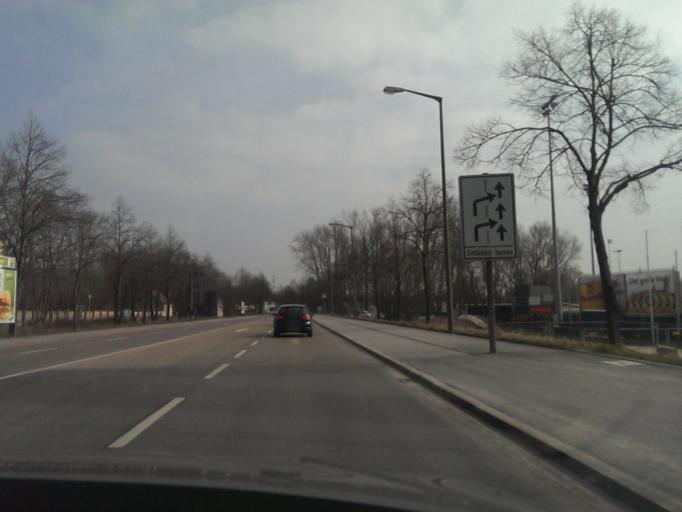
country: DE
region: Bavaria
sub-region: Upper Palatinate
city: Regensburg
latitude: 49.0270
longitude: 12.1399
